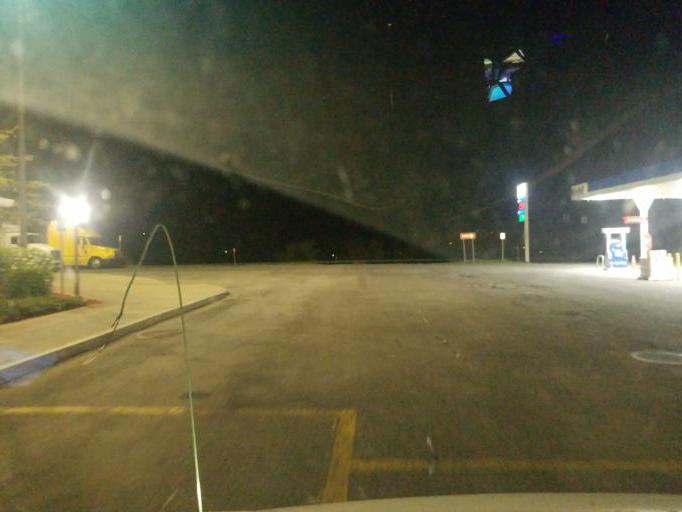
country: US
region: New York
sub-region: Montgomery County
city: Amsterdam
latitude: 42.9145
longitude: -74.1621
